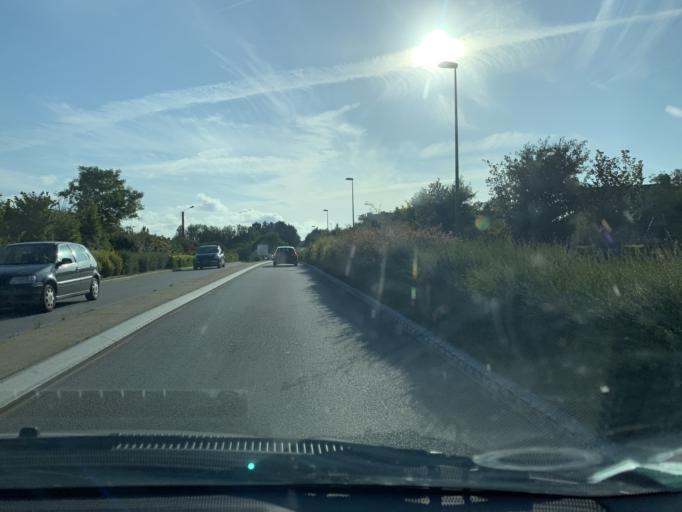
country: FR
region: Brittany
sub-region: Departement du Morbihan
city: Surzur
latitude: 47.5758
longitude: -2.6283
